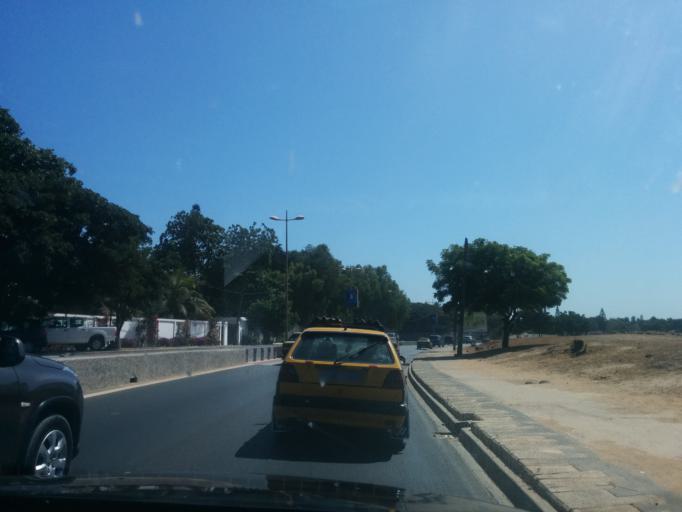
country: SN
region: Dakar
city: Mermoz Boabab
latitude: 14.6998
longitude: -17.4727
